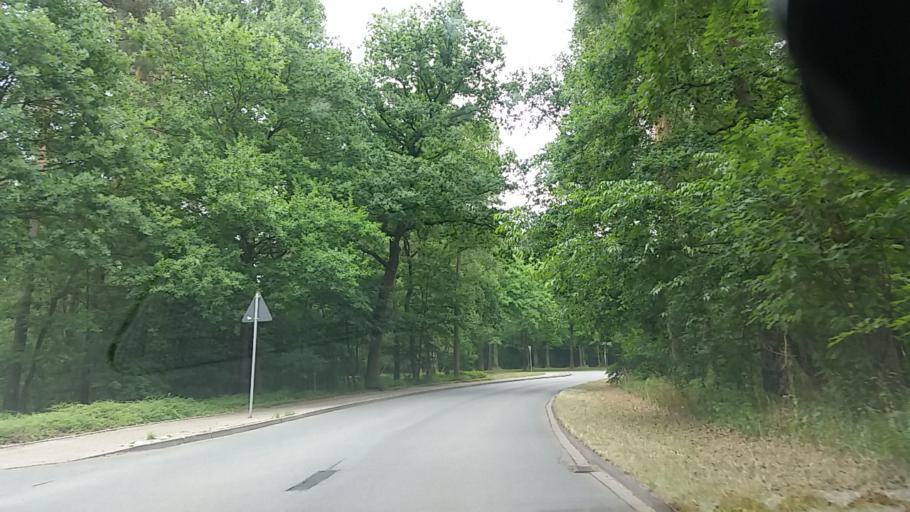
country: DE
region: Lower Saxony
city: Wolfsburg
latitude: 52.4608
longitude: 10.8002
